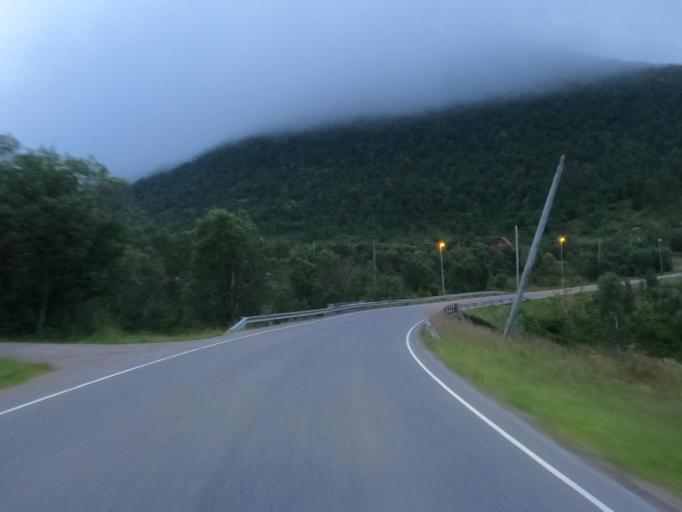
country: NO
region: Nordland
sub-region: Lodingen
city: Lodingen
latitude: 68.6159
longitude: 15.7602
